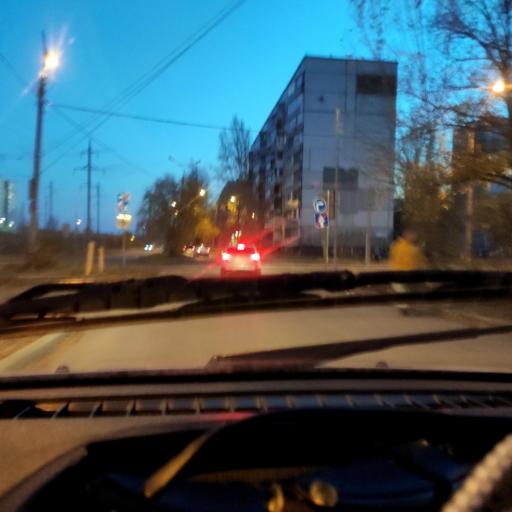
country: RU
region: Samara
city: Zhigulevsk
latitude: 53.4755
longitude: 49.5165
